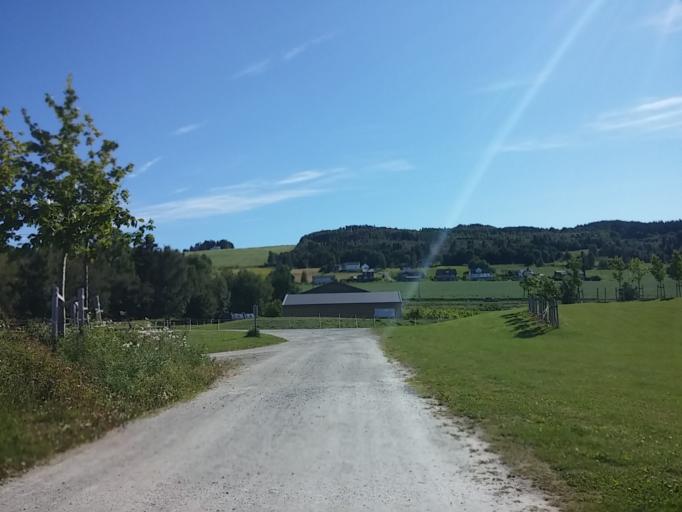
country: NO
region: Sor-Trondelag
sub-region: Malvik
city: Malvik
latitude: 63.4329
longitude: 10.7278
